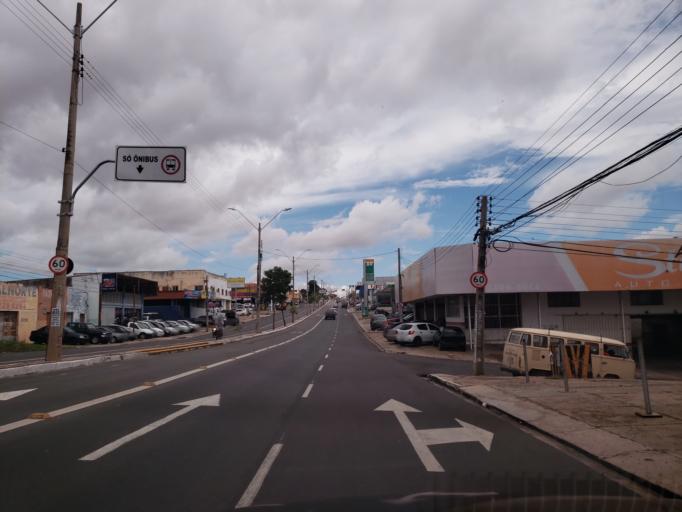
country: BR
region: Piaui
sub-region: Teresina
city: Teresina
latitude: -5.1108
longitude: -42.8070
